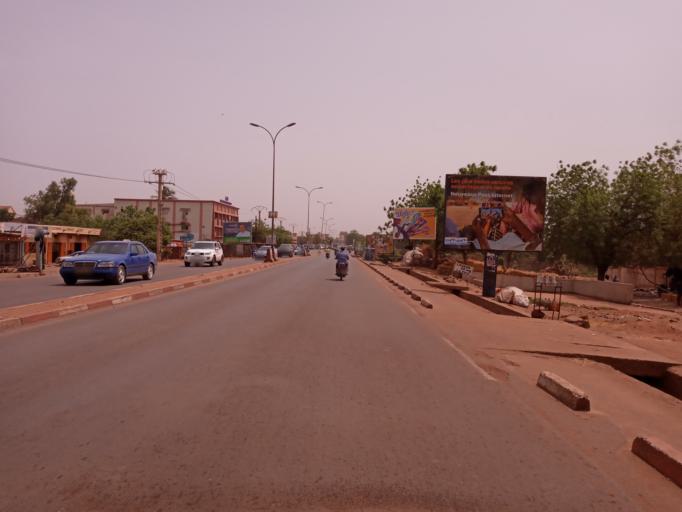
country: ML
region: Bamako
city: Bamako
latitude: 12.6594
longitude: -7.9617
